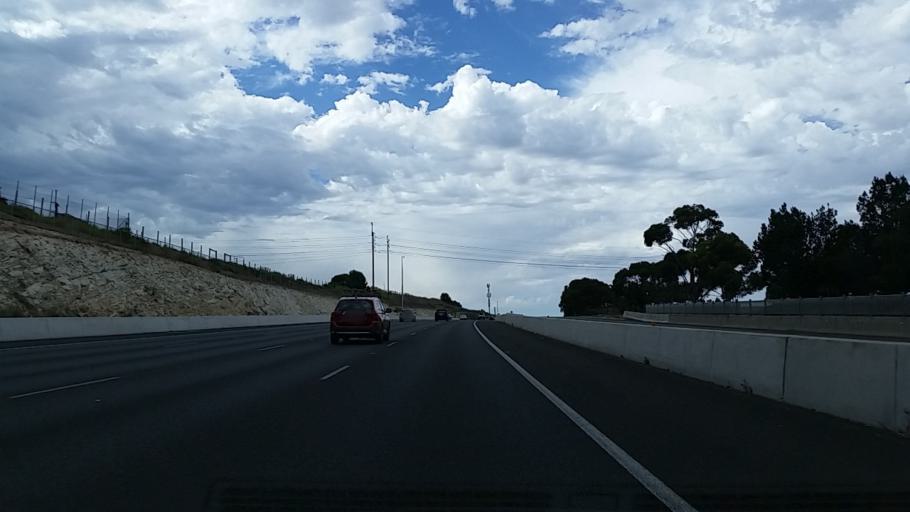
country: AU
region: South Australia
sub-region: Marion
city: Trott Park
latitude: -35.0604
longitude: 138.5451
